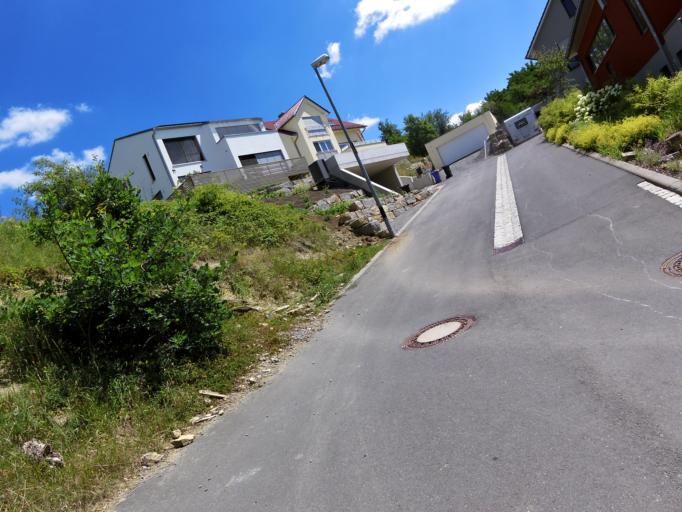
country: DE
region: Bavaria
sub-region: Regierungsbezirk Unterfranken
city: Gadheim
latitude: 49.8249
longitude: 9.9267
